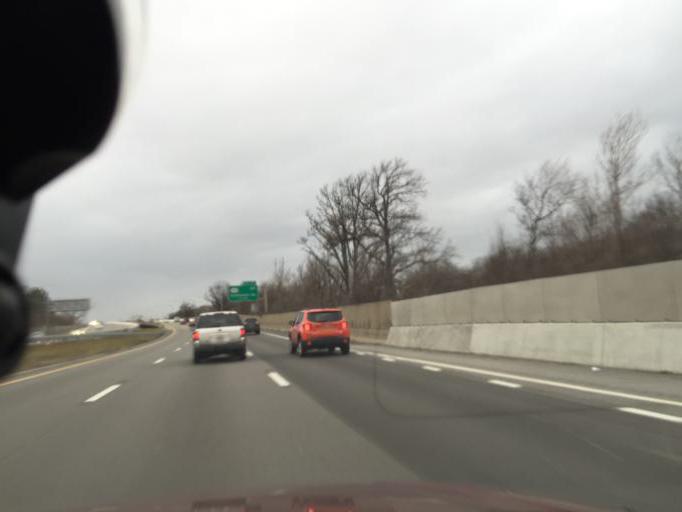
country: US
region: New York
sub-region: Monroe County
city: Rochester
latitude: 43.1186
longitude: -77.6376
